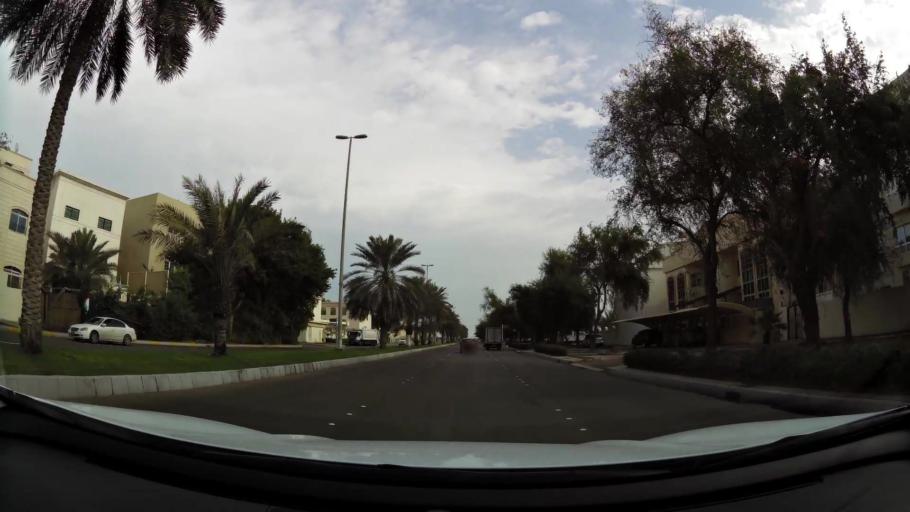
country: AE
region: Abu Dhabi
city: Abu Dhabi
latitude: 24.4441
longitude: 54.4084
